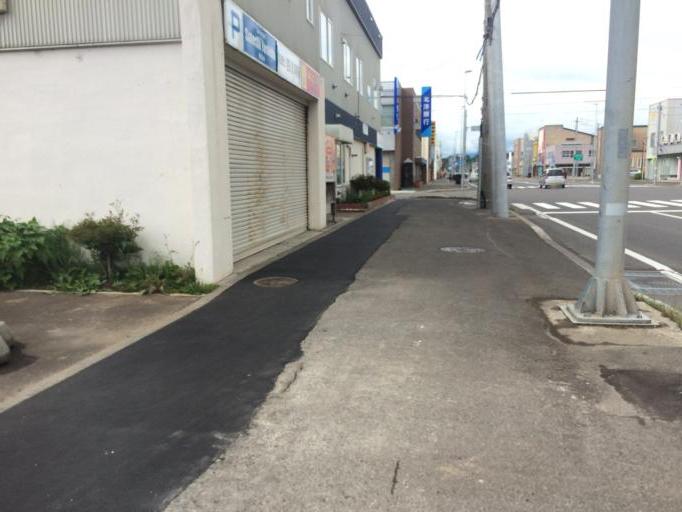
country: JP
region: Hokkaido
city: Niseko Town
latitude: 42.9011
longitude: 140.7525
